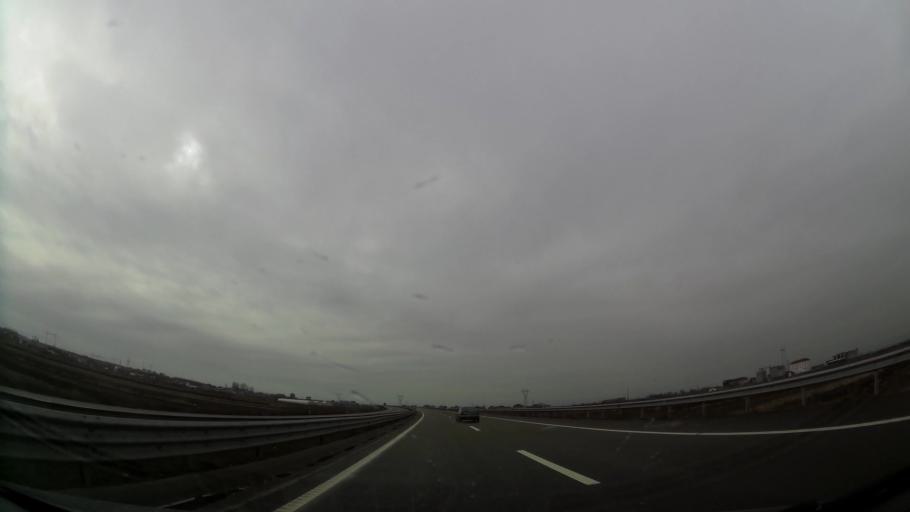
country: XK
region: Pristina
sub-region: Lipjan
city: Lipljan
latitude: 42.4807
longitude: 21.1858
